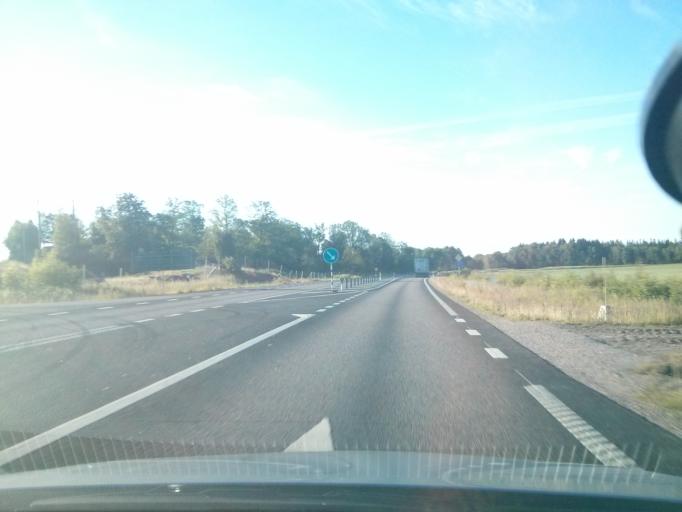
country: SE
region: Blekinge
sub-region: Ronneby Kommun
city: Kallinge
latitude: 56.2851
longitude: 15.2201
